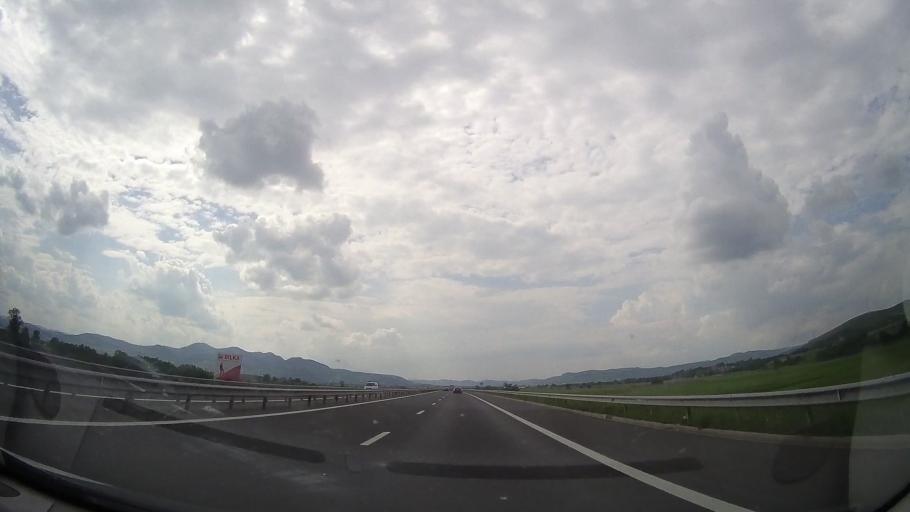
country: RO
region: Hunedoara
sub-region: Comuna Harau
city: Harau
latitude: 45.8883
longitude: 22.9733
